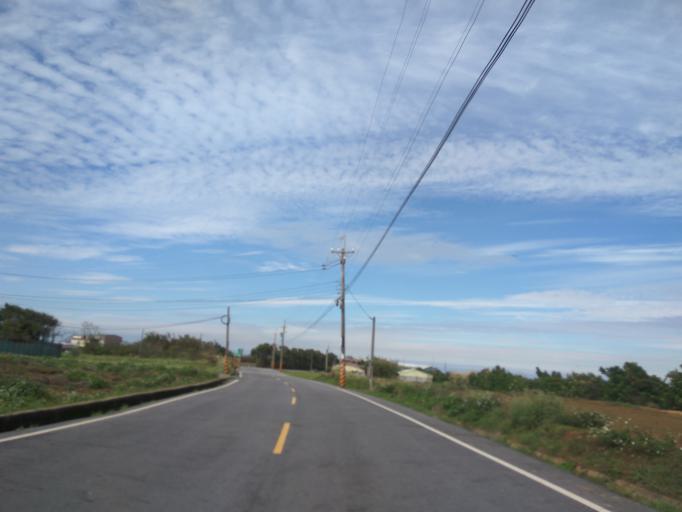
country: TW
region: Taiwan
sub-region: Hsinchu
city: Zhubei
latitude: 25.0041
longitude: 121.0826
